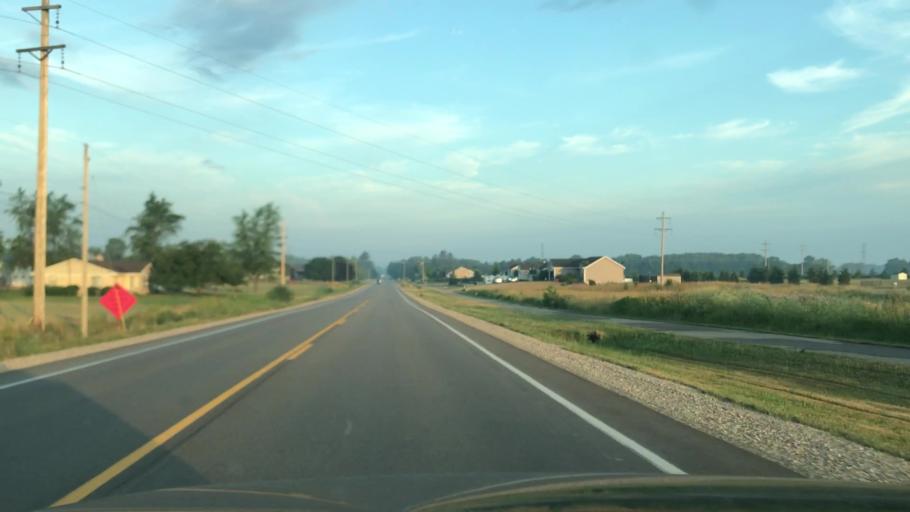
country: US
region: Michigan
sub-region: Ottawa County
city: Zeeland
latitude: 42.7833
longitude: -85.9660
